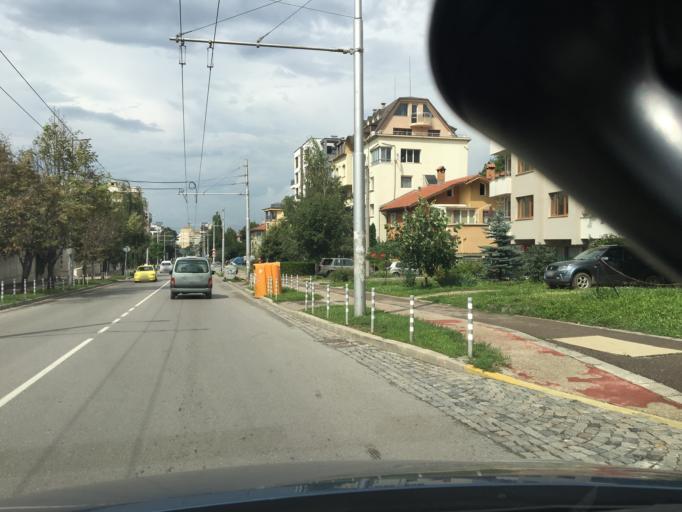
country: BG
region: Sofia-Capital
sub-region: Stolichna Obshtina
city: Sofia
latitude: 42.6616
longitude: 23.2737
